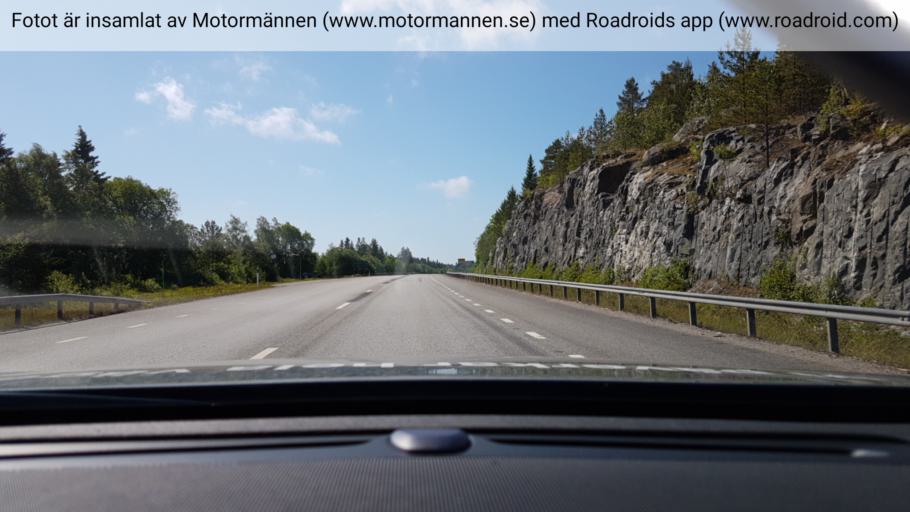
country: SE
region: Vaesterbotten
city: Obbola
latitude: 63.7497
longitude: 20.2941
